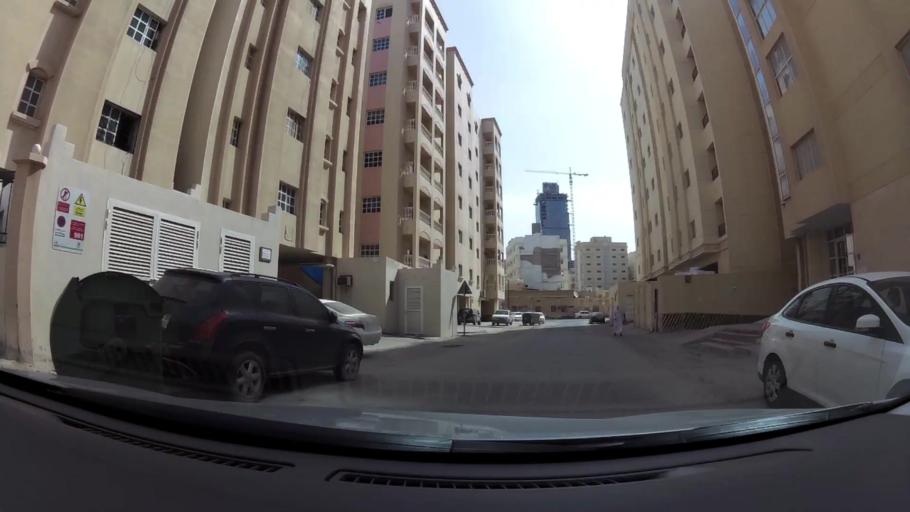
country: QA
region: Baladiyat ad Dawhah
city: Doha
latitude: 25.2860
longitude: 51.5120
